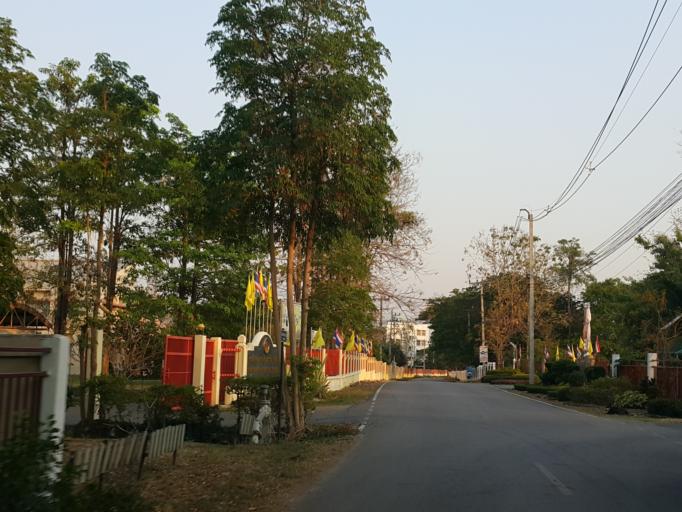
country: TH
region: Chiang Mai
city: San Sai
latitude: 18.8904
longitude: 98.9641
